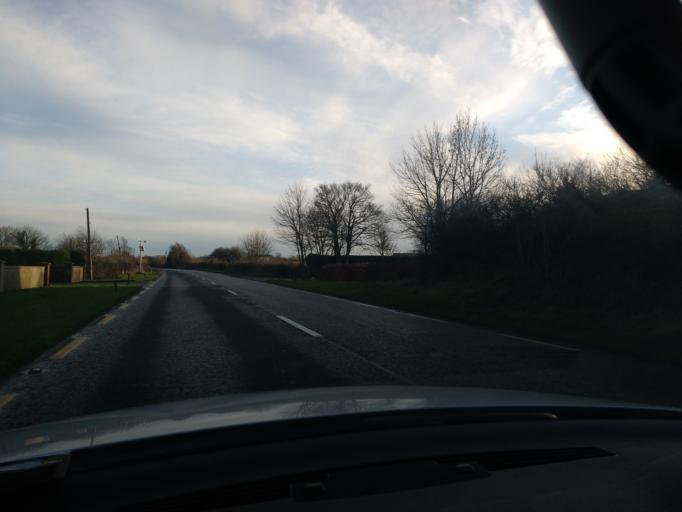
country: IE
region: Munster
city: Thurles
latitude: 52.6402
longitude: -7.7853
